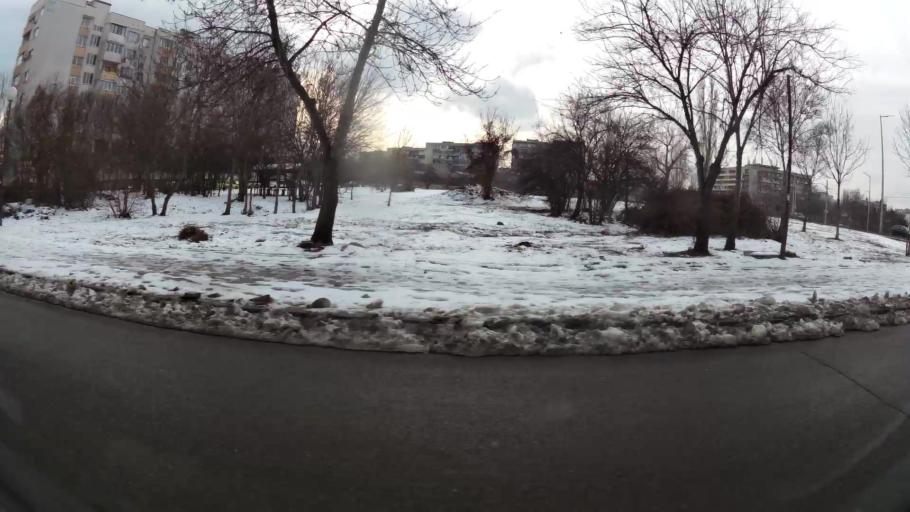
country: BG
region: Sofia-Capital
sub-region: Stolichna Obshtina
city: Sofia
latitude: 42.7006
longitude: 23.3754
